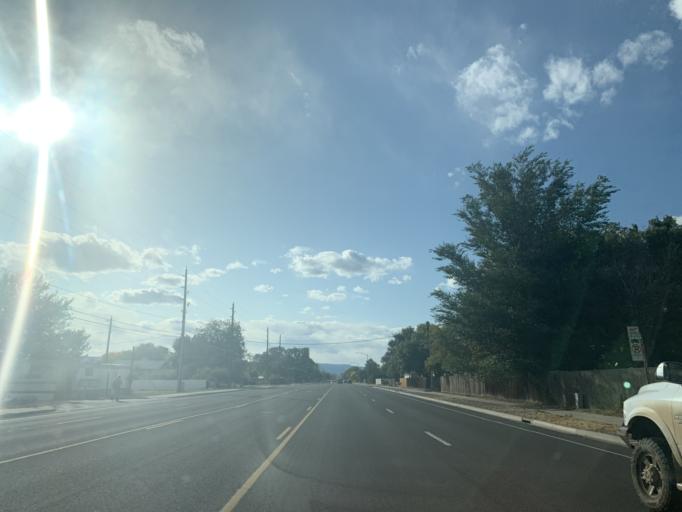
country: US
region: Colorado
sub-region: Mesa County
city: Fruitvale
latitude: 39.0919
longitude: -108.4875
